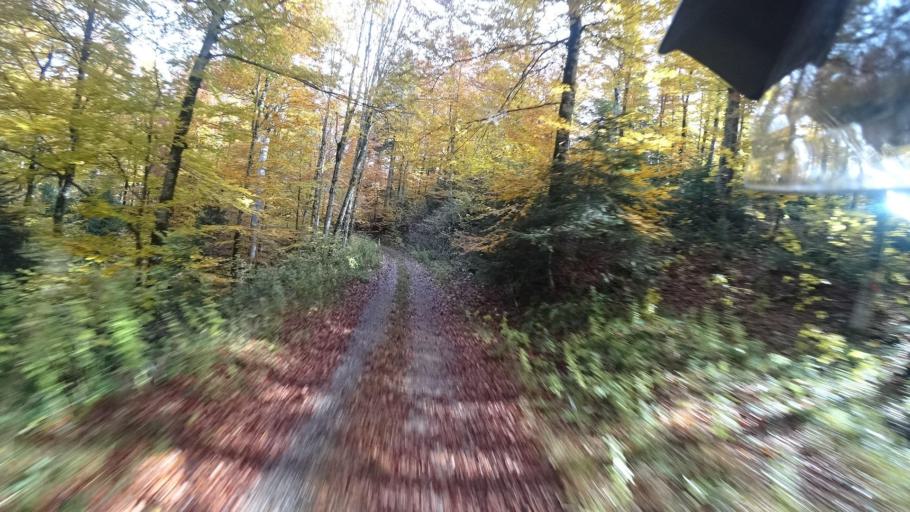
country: HR
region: Karlovacka
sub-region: Grad Ogulin
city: Ogulin
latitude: 45.2105
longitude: 15.0926
